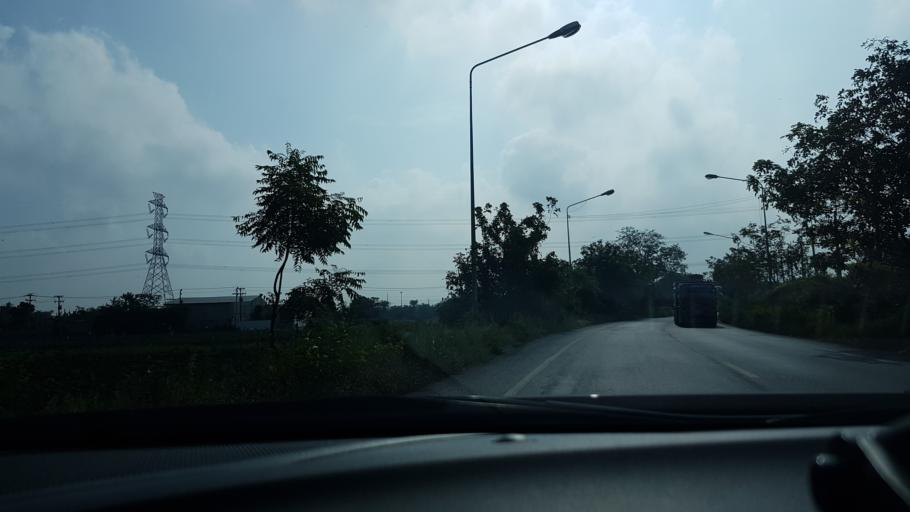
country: TH
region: Pathum Thani
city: Sam Khok
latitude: 14.1208
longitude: 100.5648
